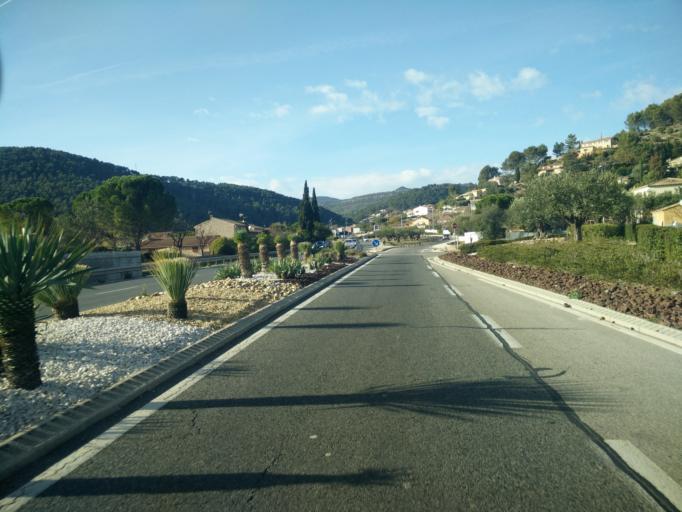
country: FR
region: Provence-Alpes-Cote d'Azur
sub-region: Departement du Var
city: Sollies-Pont
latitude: 43.1969
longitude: 6.0385
